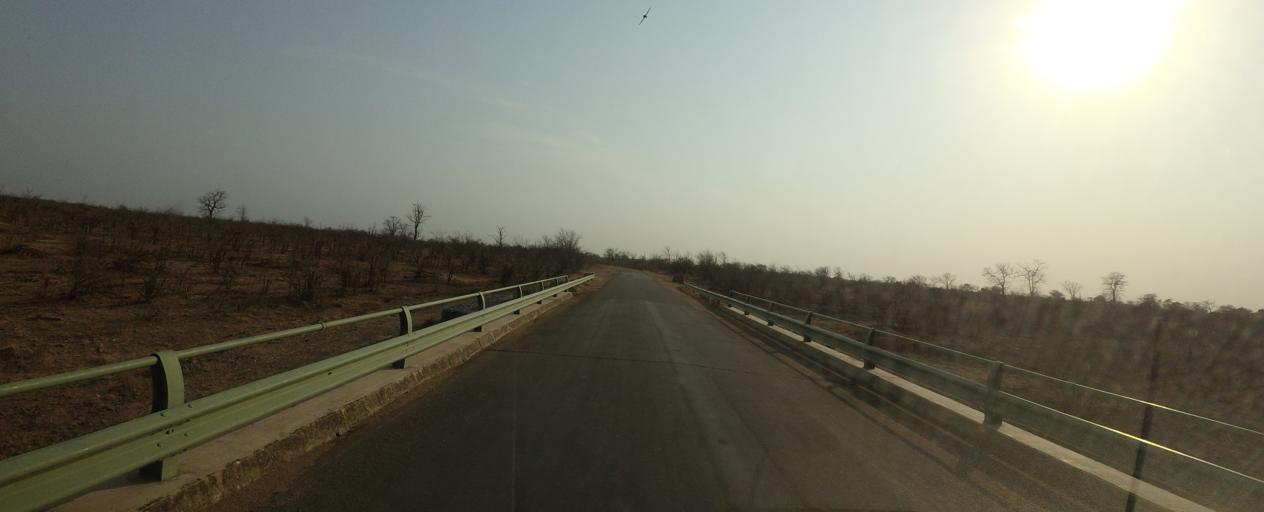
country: ZA
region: Limpopo
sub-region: Mopani District Municipality
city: Giyani
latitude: -23.0932
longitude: 31.4190
